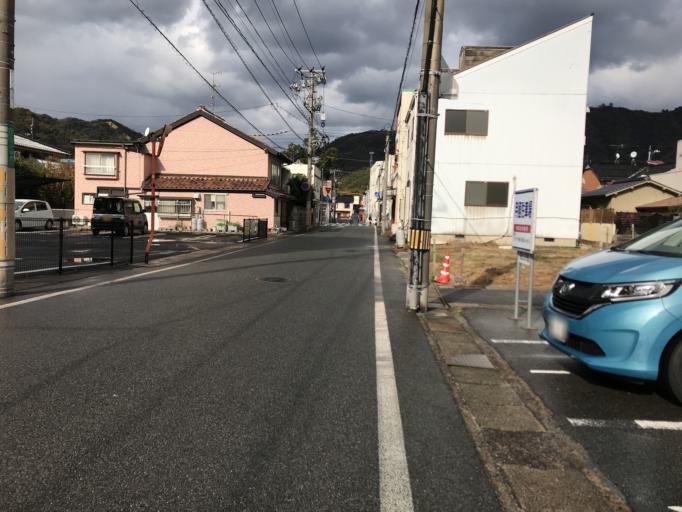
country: JP
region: Shimane
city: Sakaiminato
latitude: 35.5453
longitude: 133.2306
